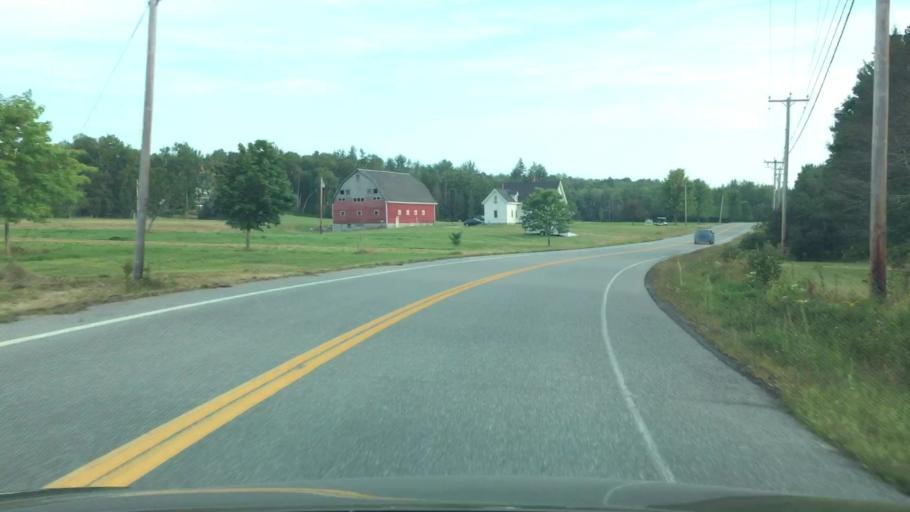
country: US
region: Maine
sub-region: Hancock County
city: Penobscot
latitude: 44.4599
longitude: -68.7805
